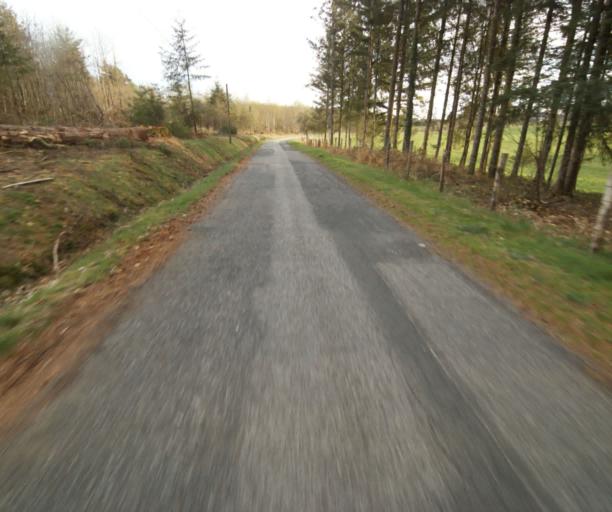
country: FR
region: Limousin
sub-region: Departement de la Correze
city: Argentat
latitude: 45.2193
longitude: 1.9615
